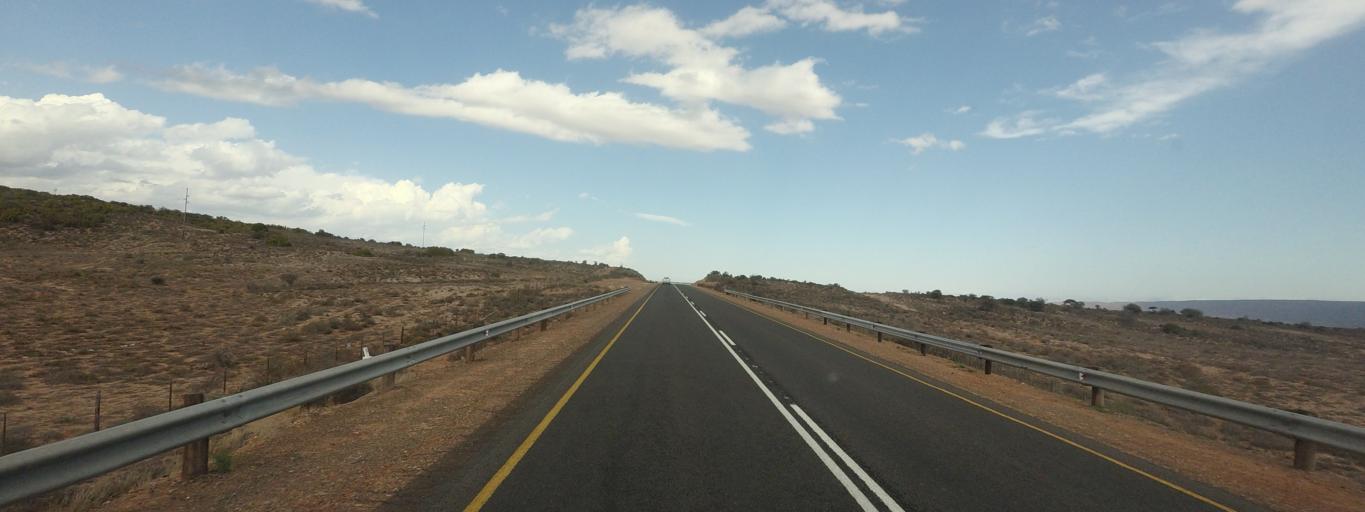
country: ZA
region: Western Cape
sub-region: Eden District Municipality
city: Oudtshoorn
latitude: -33.5707
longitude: 21.9340
